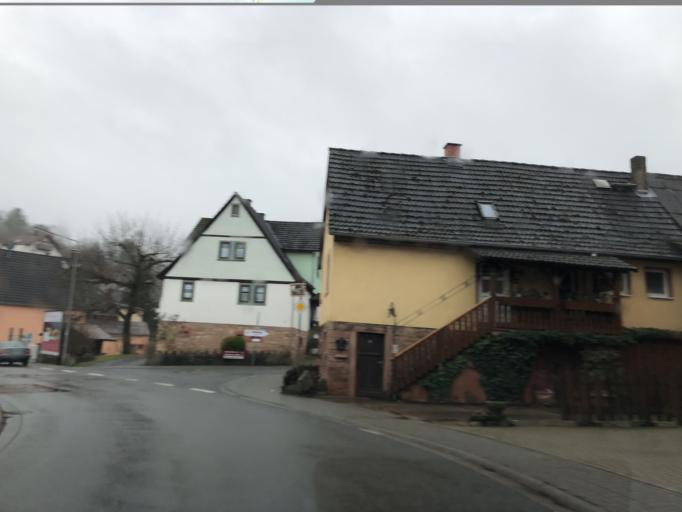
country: DE
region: Bavaria
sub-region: Regierungsbezirk Unterfranken
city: Worth am Main
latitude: 49.7865
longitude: 9.1179
